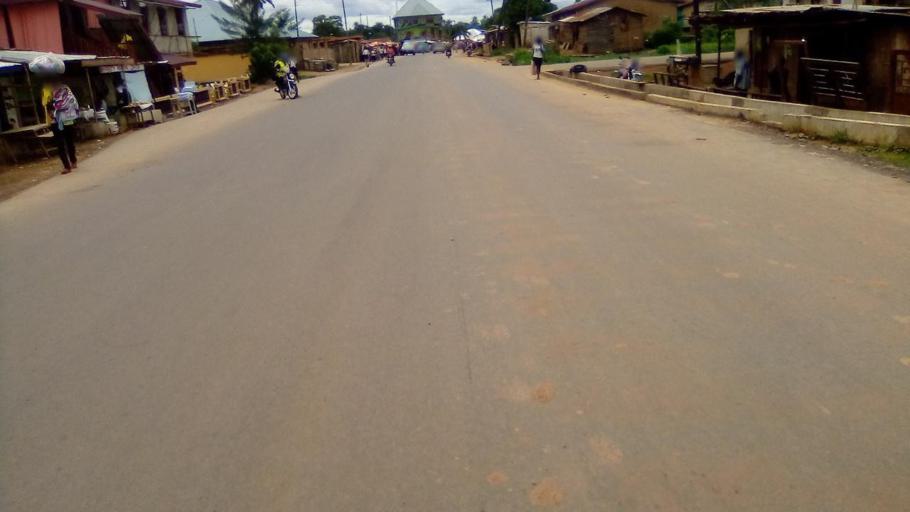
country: SL
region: Southern Province
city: Bo
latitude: 7.9517
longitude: -11.7556
